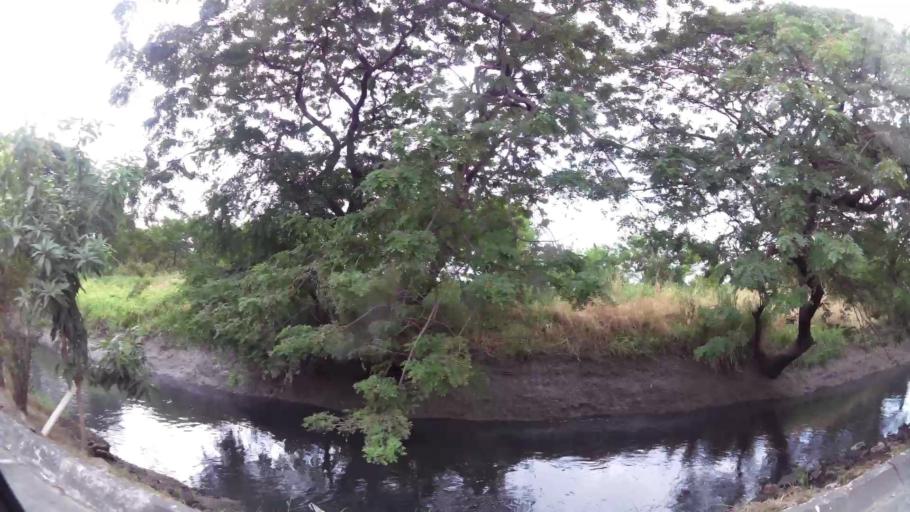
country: EC
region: Guayas
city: Eloy Alfaro
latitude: -2.1168
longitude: -79.8865
